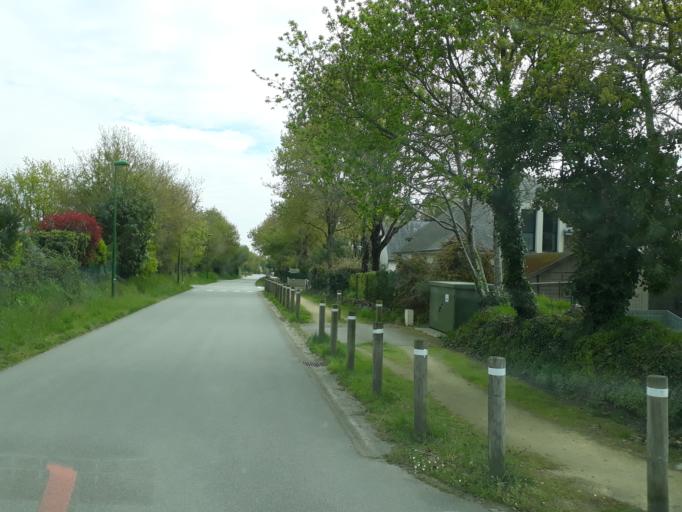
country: FR
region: Brittany
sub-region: Departement du Morbihan
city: Surzur
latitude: 47.5821
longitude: -2.6446
